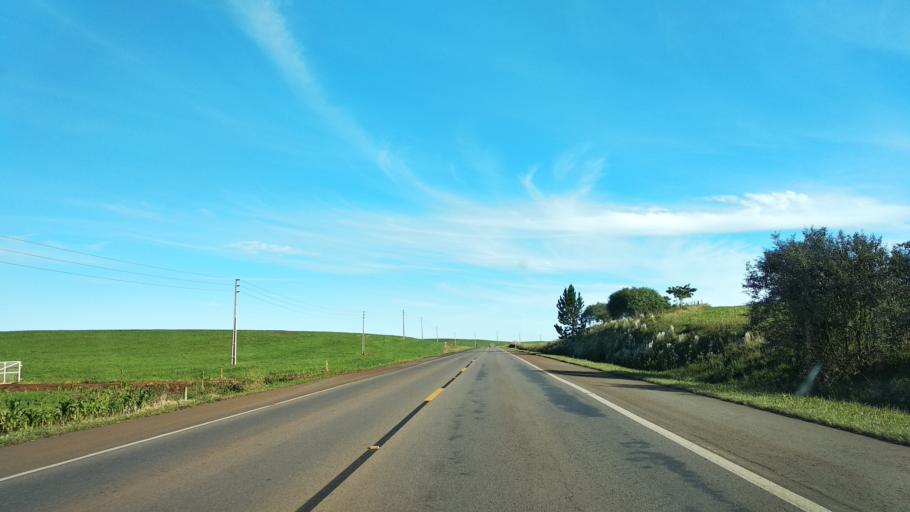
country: BR
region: Santa Catarina
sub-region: Celso Ramos
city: Celso Ramos
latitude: -27.5180
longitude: -51.3507
